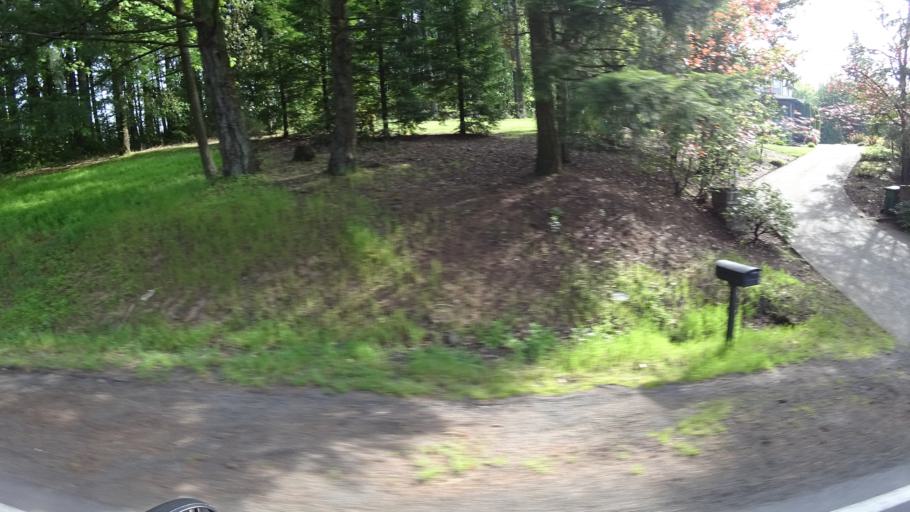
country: US
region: Oregon
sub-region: Washington County
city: Aloha
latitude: 45.4393
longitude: -122.8555
